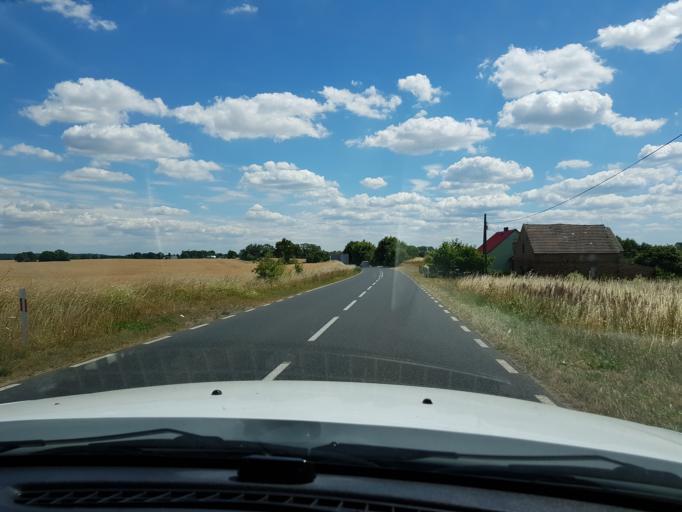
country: PL
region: West Pomeranian Voivodeship
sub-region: Powiat mysliborski
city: Mysliborz
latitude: 52.9060
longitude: 14.9305
